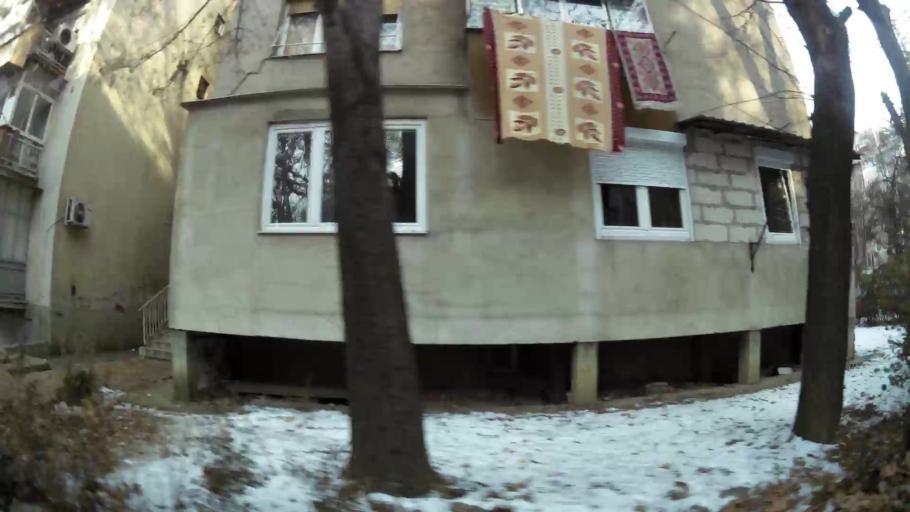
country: MK
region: Cair
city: Cair
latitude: 42.0169
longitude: 21.4320
